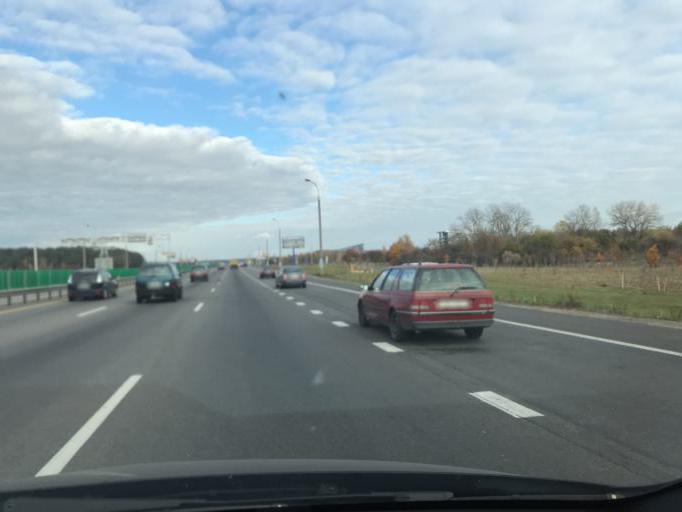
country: BY
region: Minsk
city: Zhdanovichy
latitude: 53.9461
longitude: 27.4398
